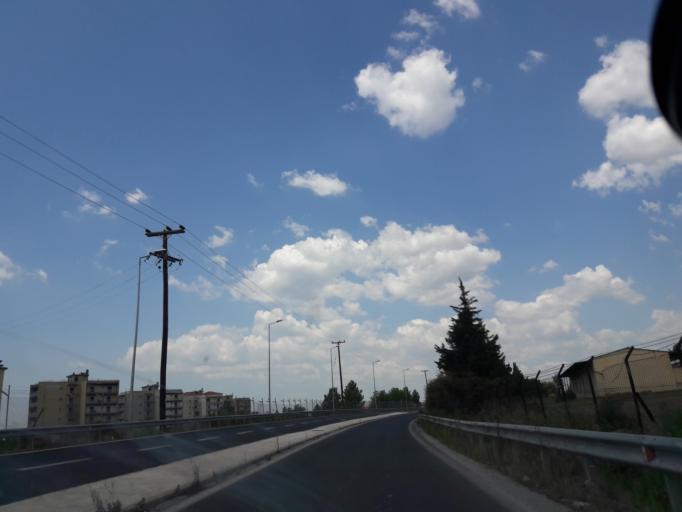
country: GR
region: Central Macedonia
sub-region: Nomos Thessalonikis
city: Thermi
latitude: 40.5336
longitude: 23.0386
